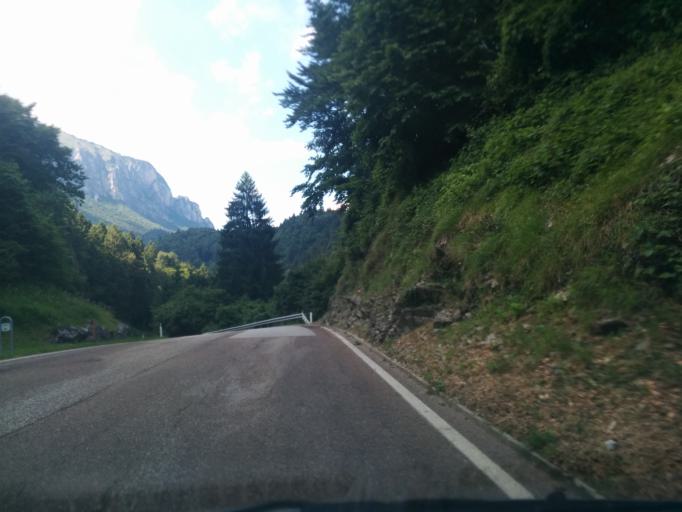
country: IT
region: Trentino-Alto Adige
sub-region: Provincia di Trento
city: Tenno
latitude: 45.9477
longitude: 10.8121
